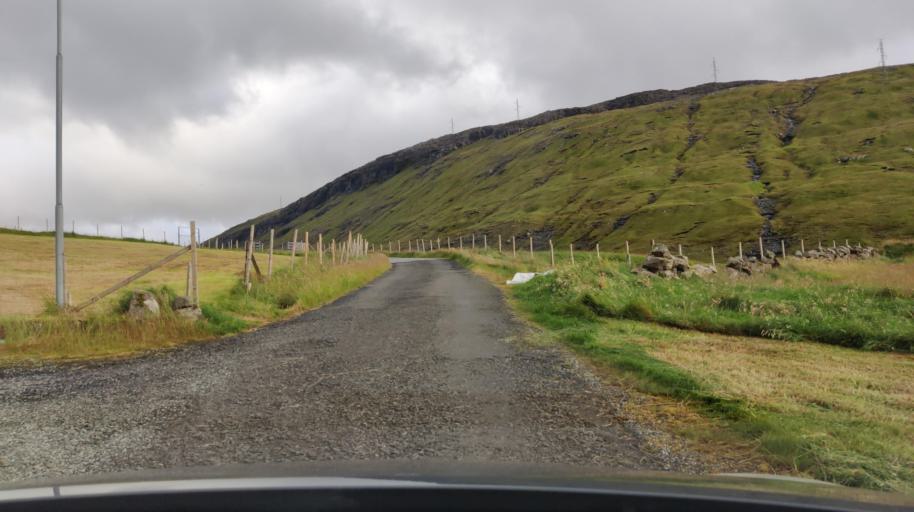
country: FO
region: Streymoy
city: Vestmanna
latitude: 62.1534
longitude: -7.1390
